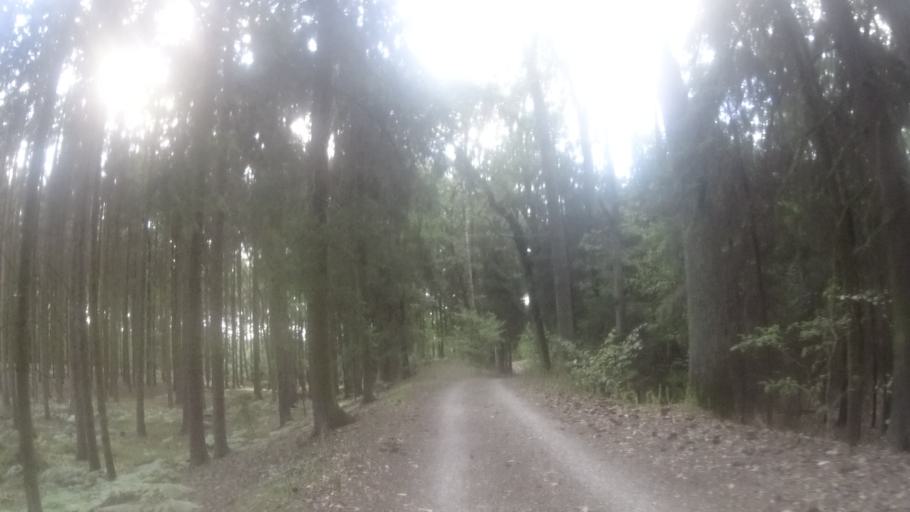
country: CZ
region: Kralovehradecky
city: Trebechovice pod Orebem
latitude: 50.1790
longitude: 16.0294
